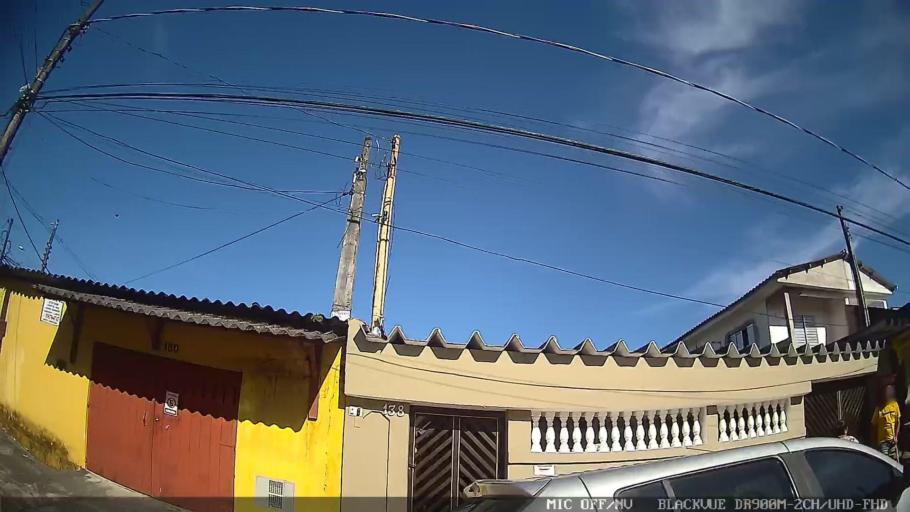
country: BR
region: Sao Paulo
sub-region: Santos
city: Santos
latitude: -23.9370
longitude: -46.2868
